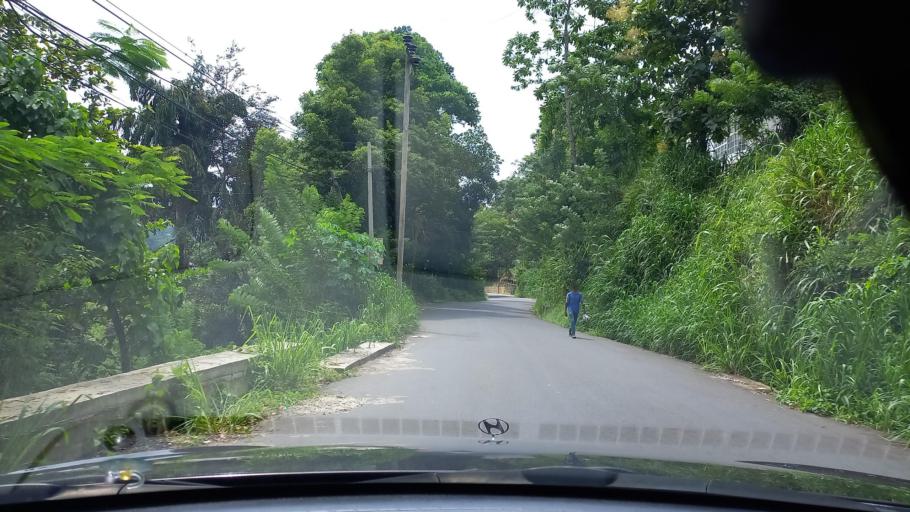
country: LK
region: Central
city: Kandy
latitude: 7.2360
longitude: 80.6026
